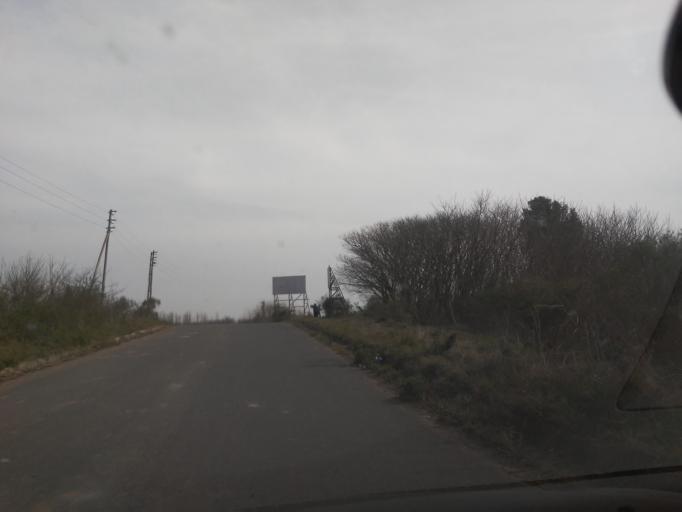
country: AR
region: Buenos Aires
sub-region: Partido de Marcos Paz
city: Marcos Paz
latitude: -34.6746
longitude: -58.8622
